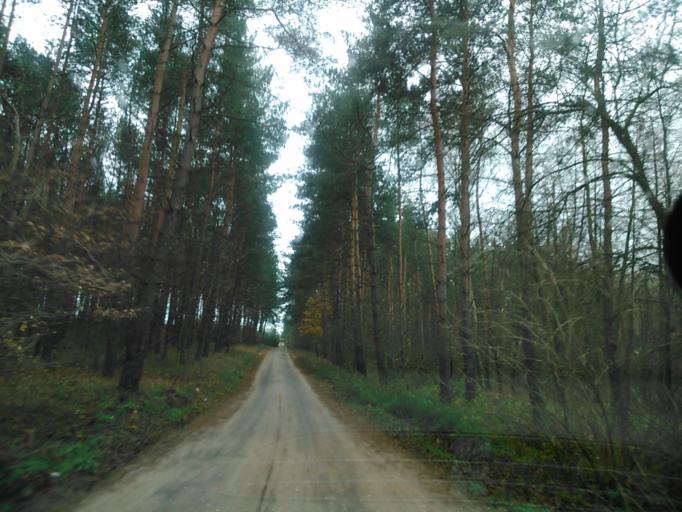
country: PL
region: Kujawsko-Pomorskie
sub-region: Powiat golubsko-dobrzynski
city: Golub-Dobrzyn
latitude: 53.1119
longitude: 19.0967
